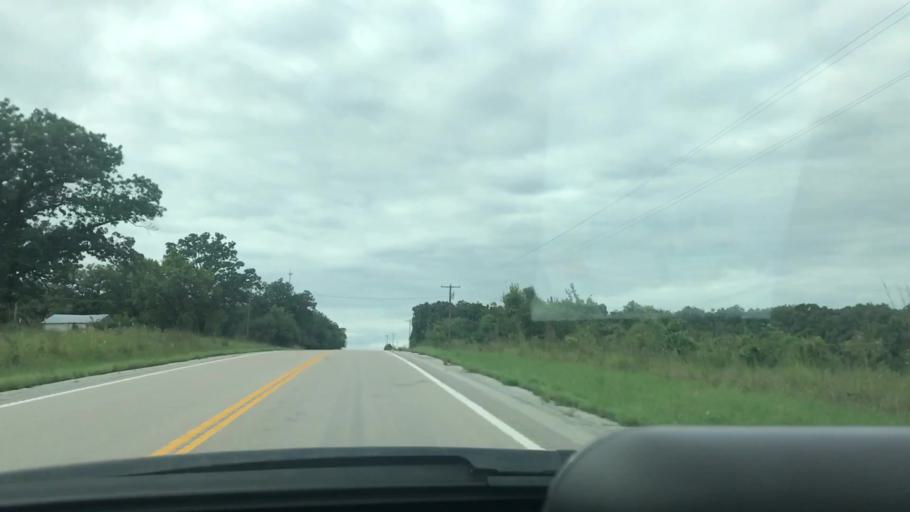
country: US
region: Missouri
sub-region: Benton County
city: Warsaw
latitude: 38.1403
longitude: -93.2865
